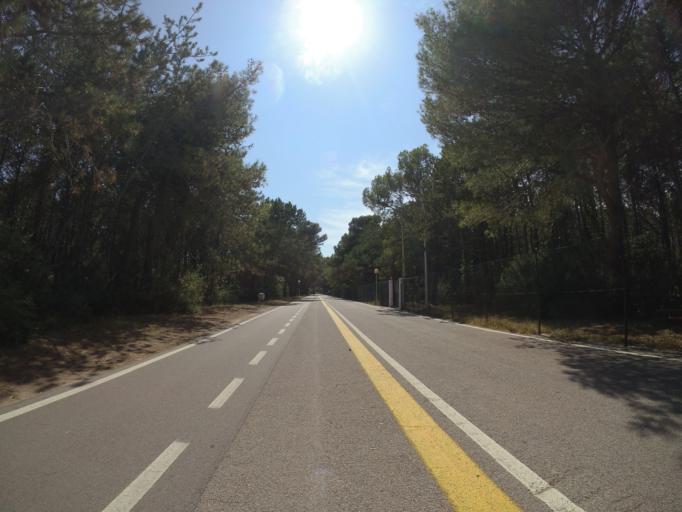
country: IT
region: Friuli Venezia Giulia
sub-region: Provincia di Udine
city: Lignano Sabbiadoro
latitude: 45.6738
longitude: 13.1207
